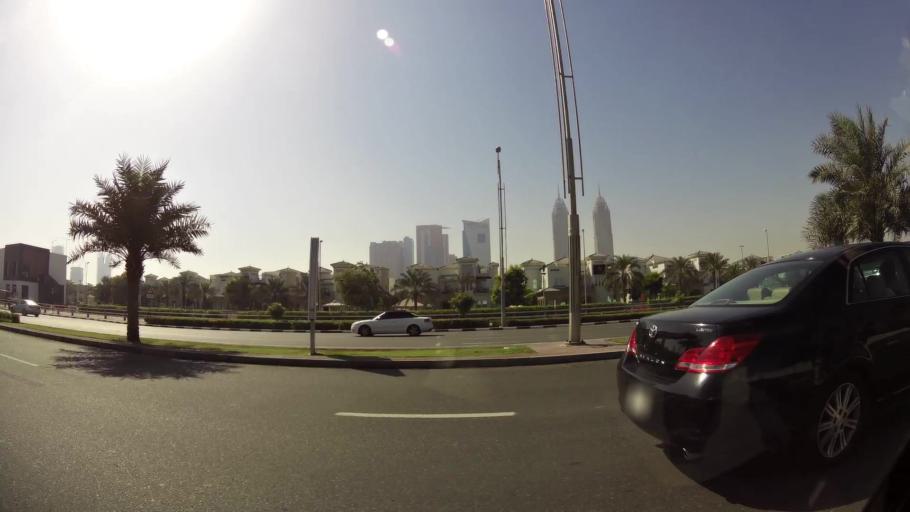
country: AE
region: Dubai
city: Dubai
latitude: 25.1073
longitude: 55.1638
